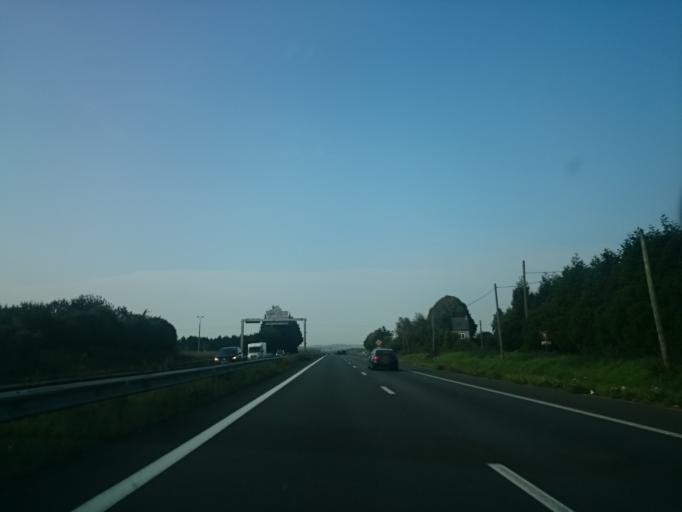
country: FR
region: Brittany
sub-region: Departement des Cotes-d'Armor
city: Lamballe
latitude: 48.4469
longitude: -2.4812
